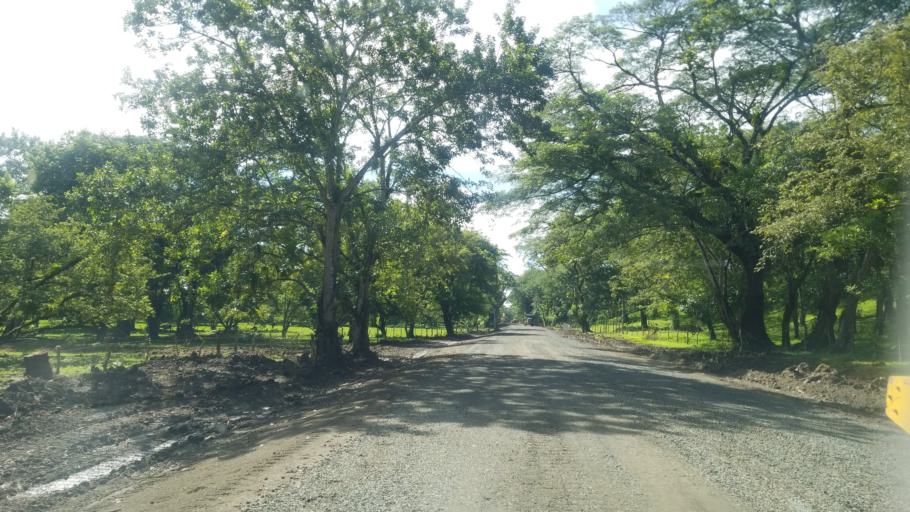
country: CR
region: Alajuela
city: San Jose
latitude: 11.0961
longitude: -85.2670
